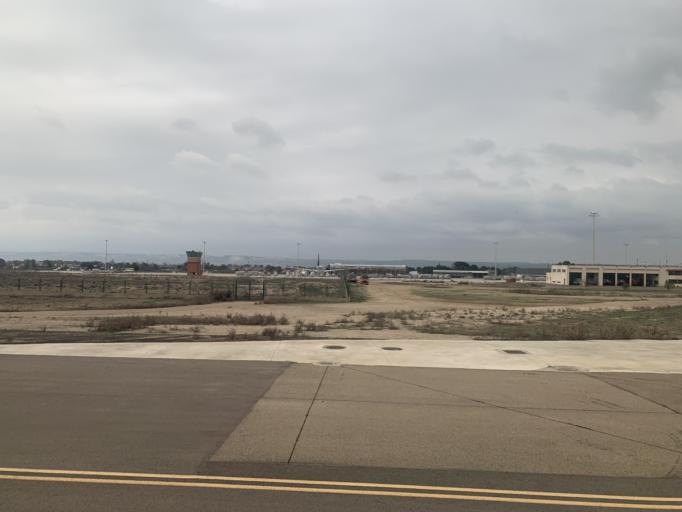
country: ES
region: Aragon
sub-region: Provincia de Zaragoza
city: Utebo
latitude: 41.6615
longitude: -1.0156
